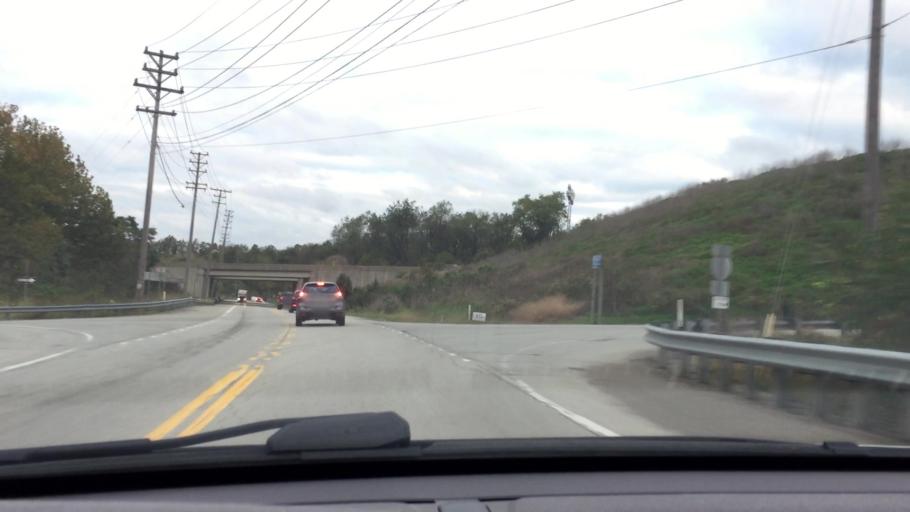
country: US
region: Pennsylvania
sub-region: Washington County
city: Houston
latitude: 40.2445
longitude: -80.1986
